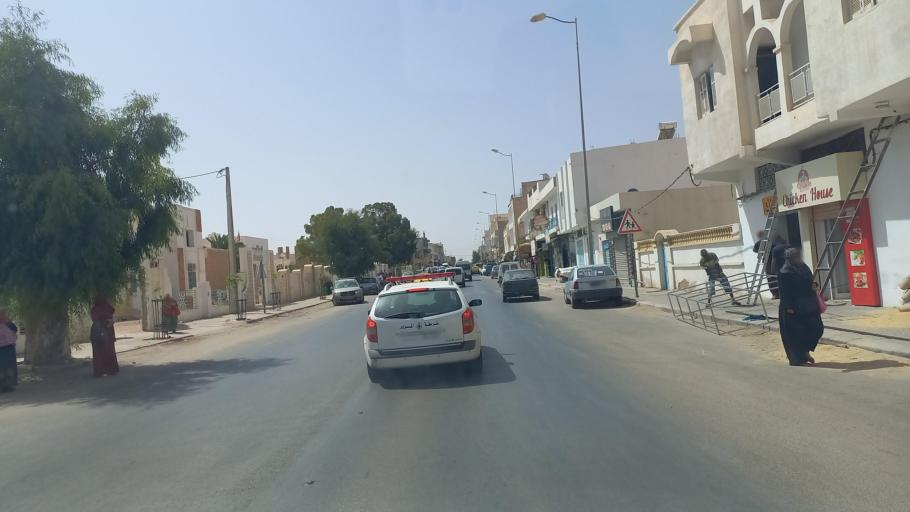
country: TN
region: Madanin
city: Medenine
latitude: 33.3359
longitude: 10.4856
